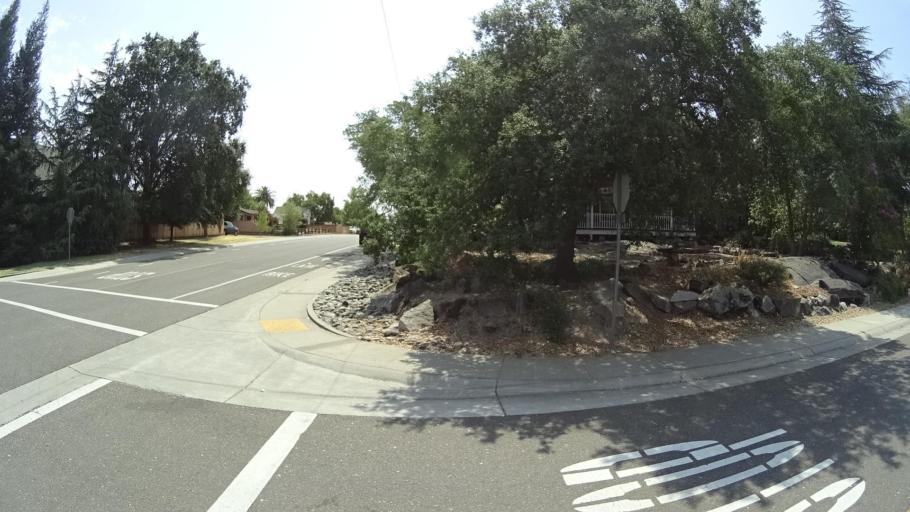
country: US
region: California
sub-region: Placer County
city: Rocklin
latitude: 38.7913
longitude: -121.2340
